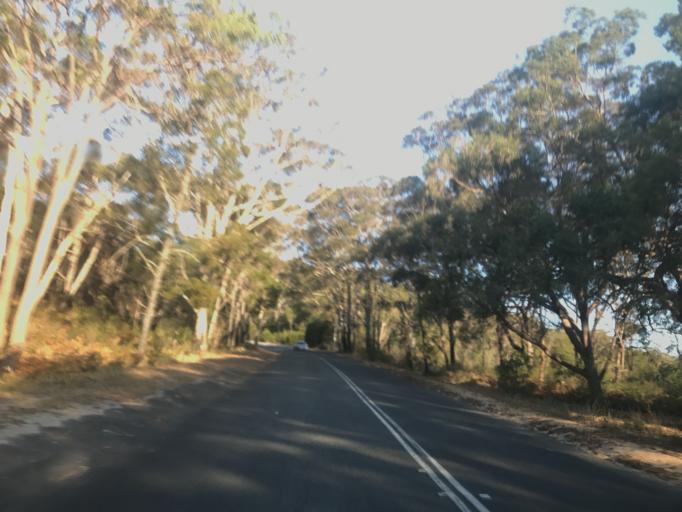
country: AU
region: Queensland
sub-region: Redland
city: Victoria Point
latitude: -27.5030
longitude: 153.4119
